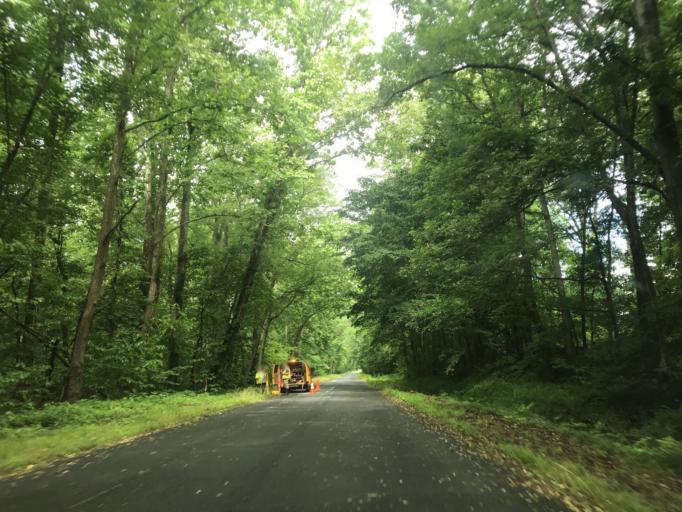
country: US
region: Maryland
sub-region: Caroline County
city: Ridgely
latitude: 38.9190
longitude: -75.9637
